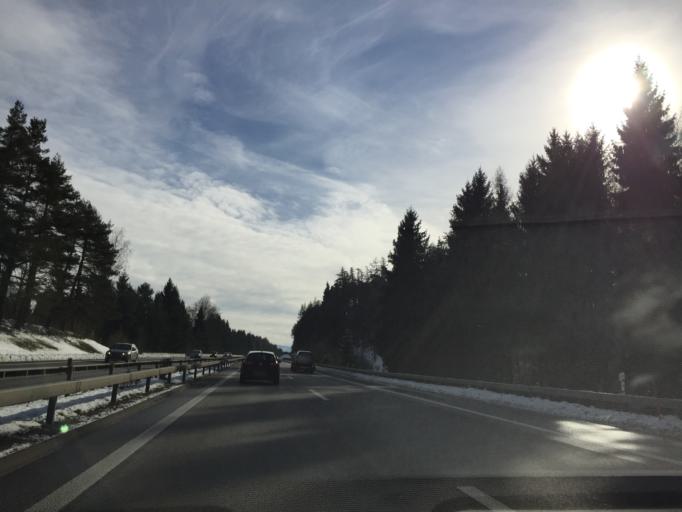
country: CH
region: Zurich
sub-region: Bezirk Horgen
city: Oberrieden / Berg
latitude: 47.2765
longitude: 8.5650
